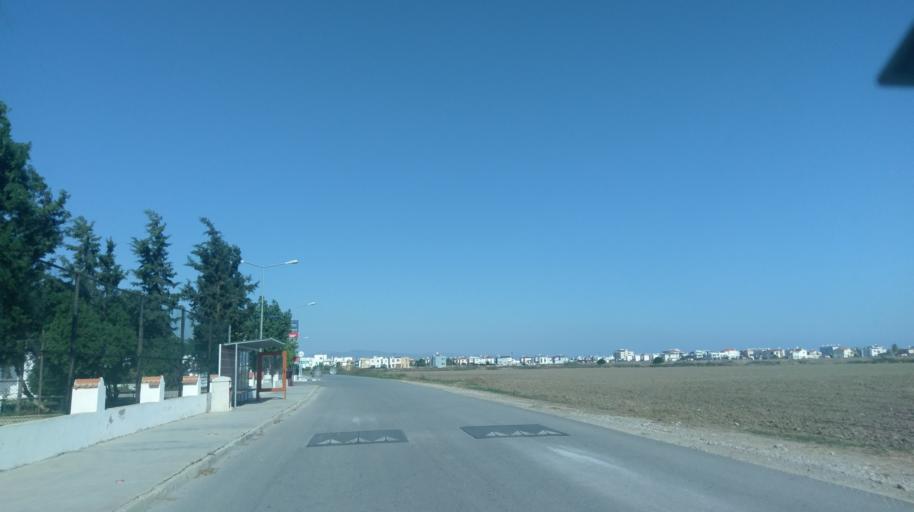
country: CY
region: Ammochostos
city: Acheritou
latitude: 35.1509
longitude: 33.8850
